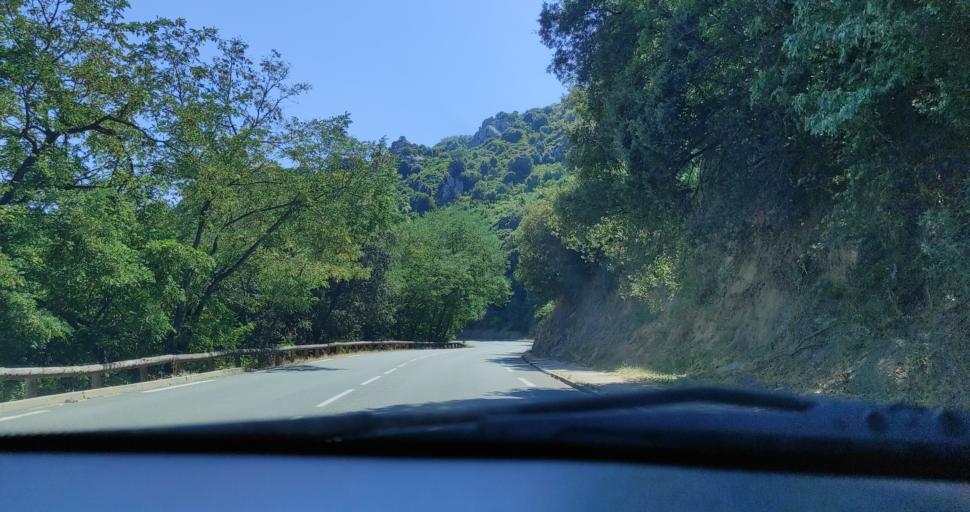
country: FR
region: Corsica
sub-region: Departement de la Corse-du-Sud
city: Sartene
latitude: 41.6167
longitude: 8.9572
